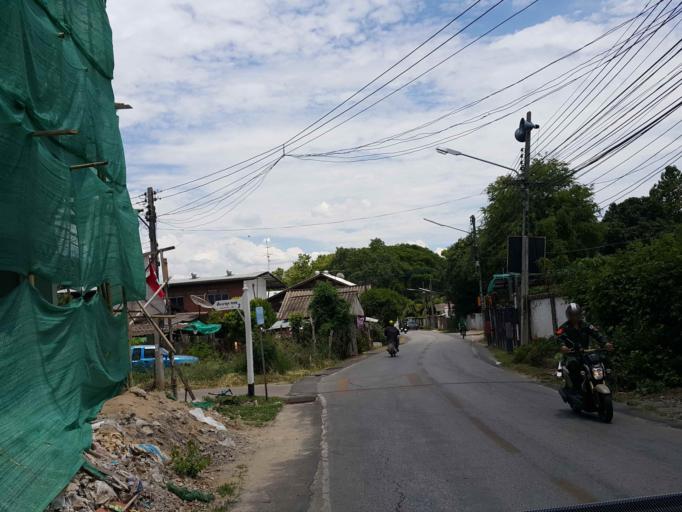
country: TH
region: Chiang Mai
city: Chiang Mai
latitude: 18.7811
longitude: 99.0148
